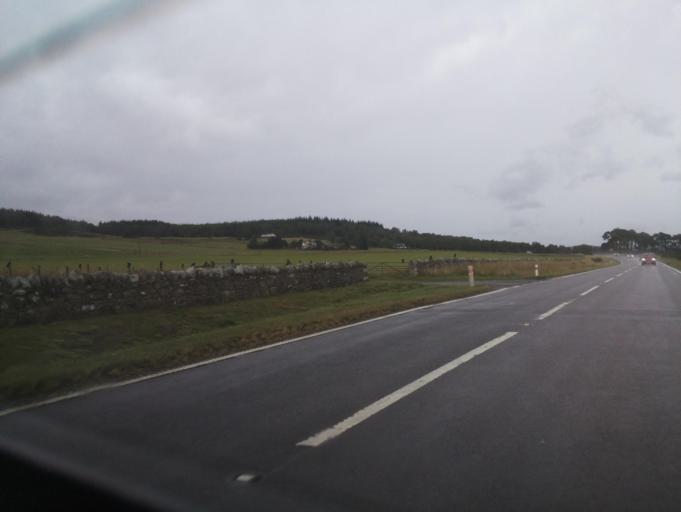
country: GB
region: Scotland
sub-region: Highland
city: Grantown on Spey
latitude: 57.2747
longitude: -3.7148
